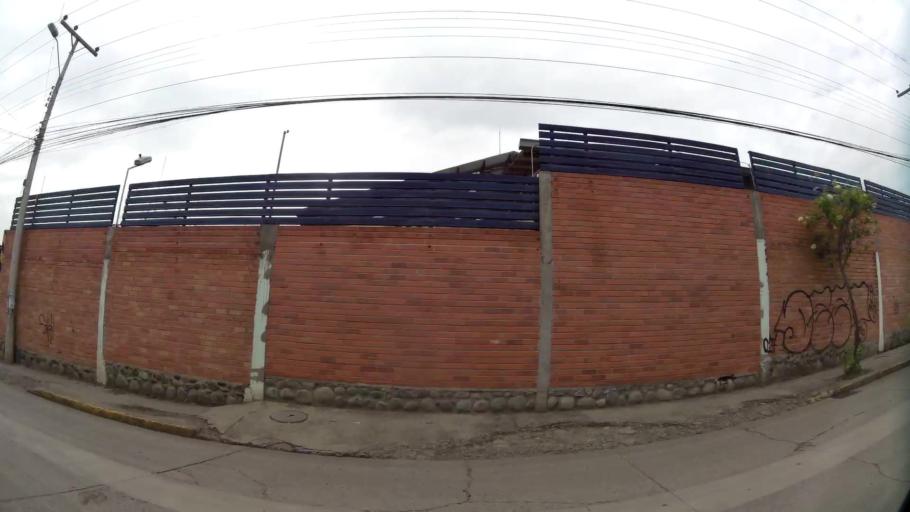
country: EC
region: Azuay
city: Cuenca
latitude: -2.9122
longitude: -79.0343
